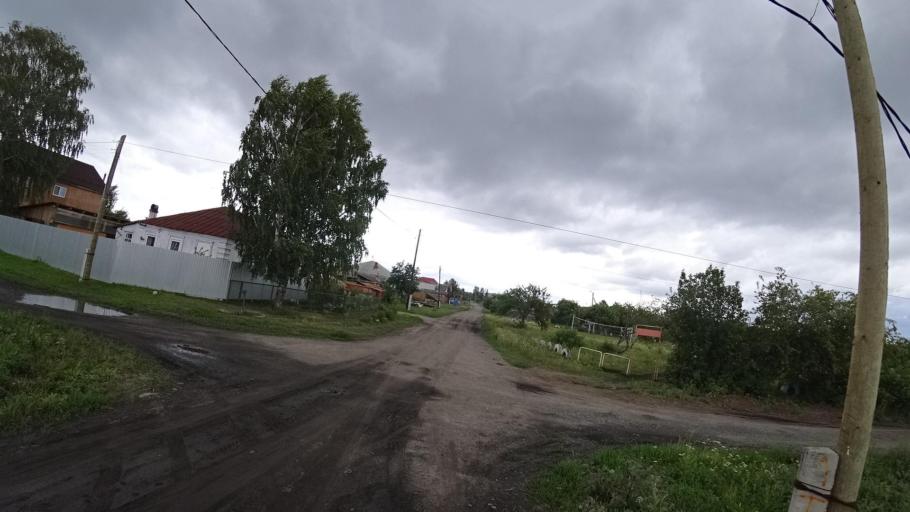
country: RU
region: Sverdlovsk
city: Kamyshlov
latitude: 56.8551
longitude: 62.6893
